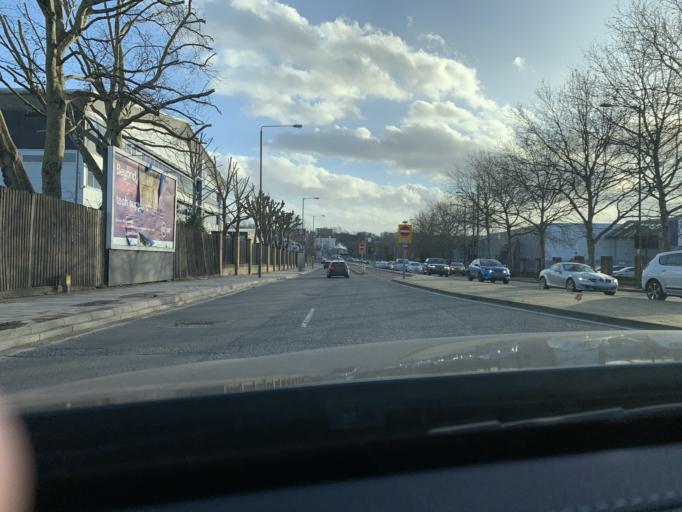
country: GB
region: England
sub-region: Greater London
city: Blackheath
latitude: 51.4900
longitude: 0.0301
